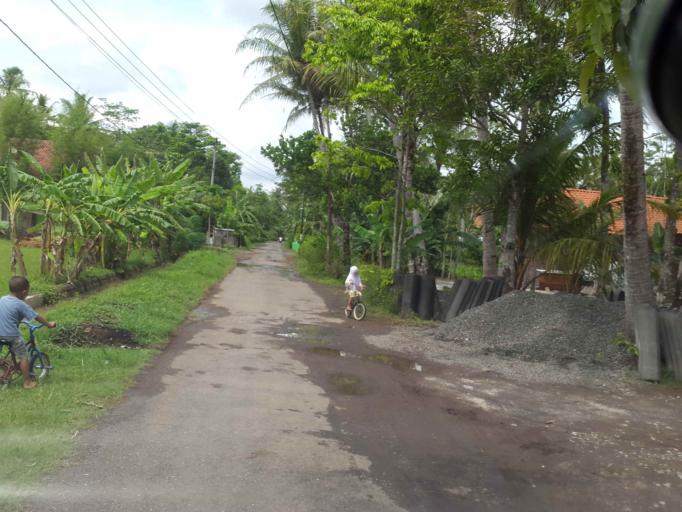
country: ID
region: Central Java
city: Kutoarjo
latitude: -7.7556
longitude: 109.9123
